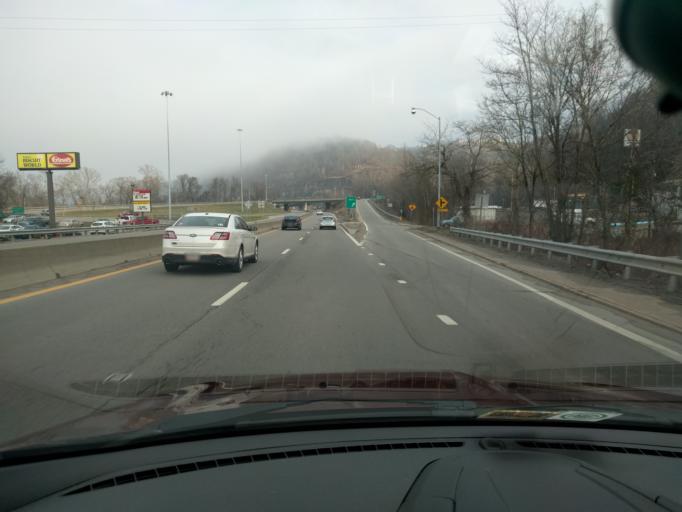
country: US
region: West Virginia
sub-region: Kanawha County
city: Rand
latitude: 38.3130
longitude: -81.5590
